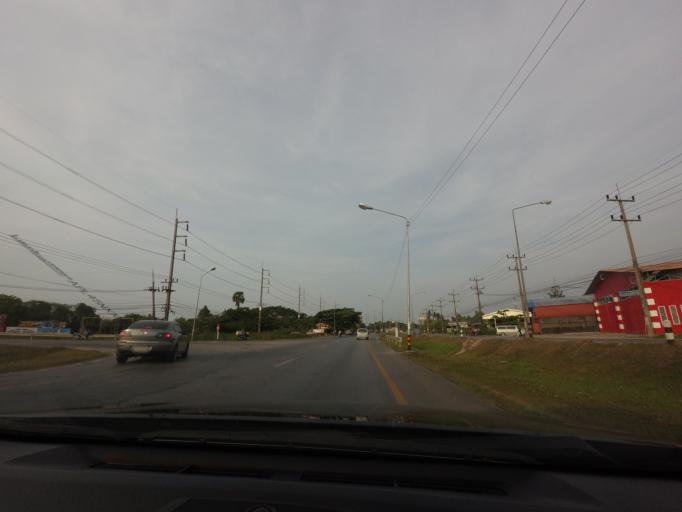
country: TH
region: Pattani
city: Pattani
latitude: 6.8688
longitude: 101.2759
